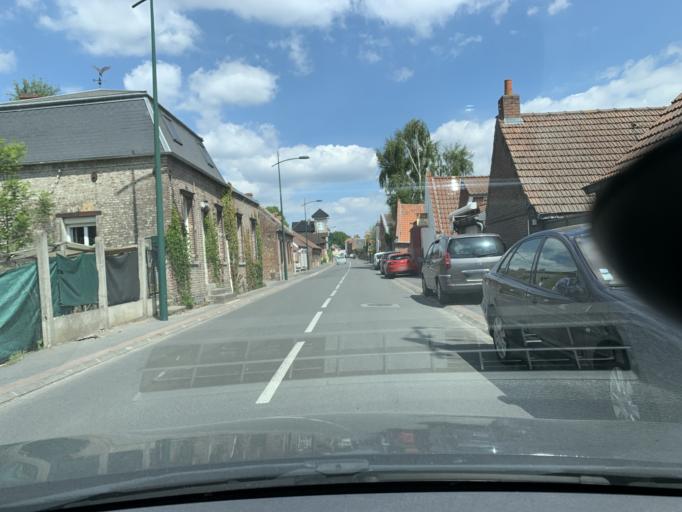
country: FR
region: Nord-Pas-de-Calais
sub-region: Departement du Nord
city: Arleux
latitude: 50.2750
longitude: 3.1008
